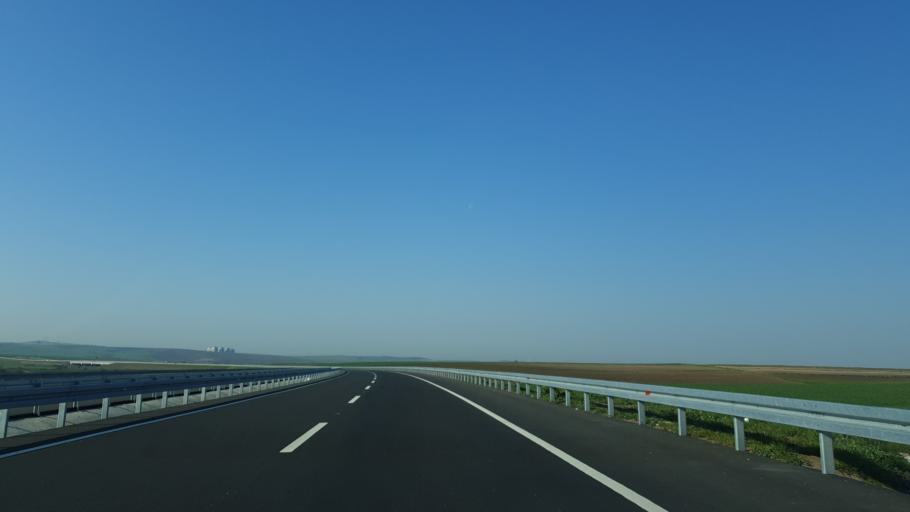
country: TR
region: Tekirdag
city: Marmaracik
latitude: 41.1941
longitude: 27.7508
